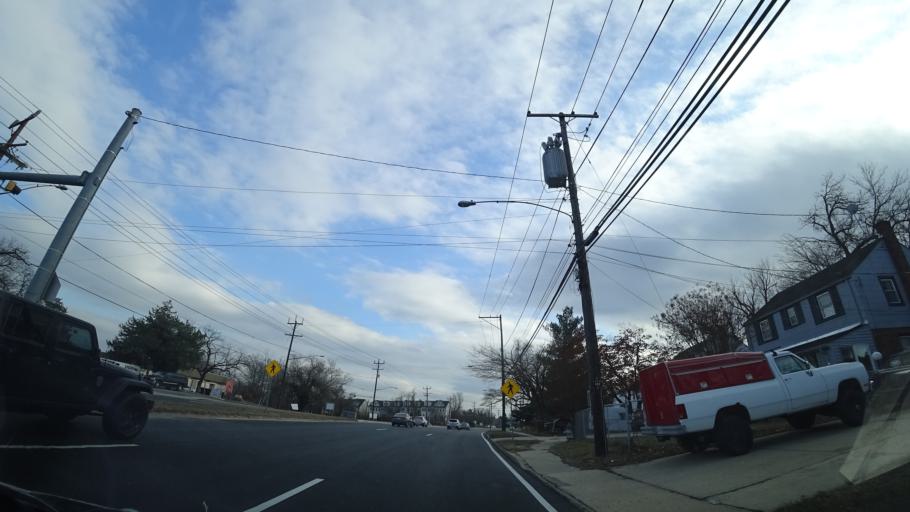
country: US
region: Maryland
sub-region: Montgomery County
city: Four Corners
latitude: 39.0091
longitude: -76.9992
